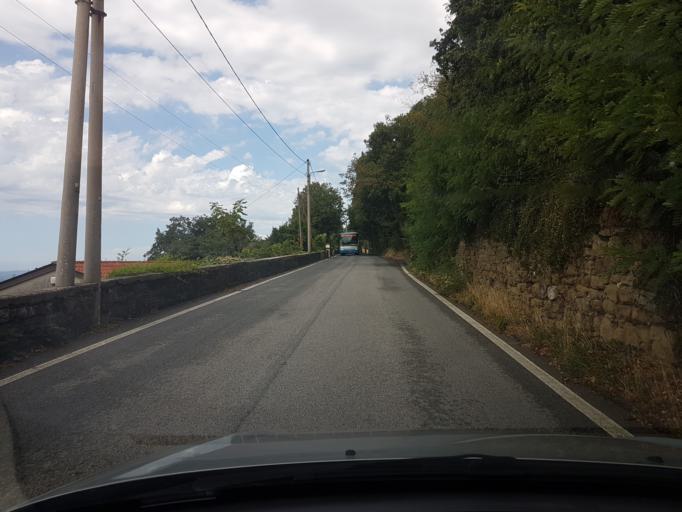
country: IT
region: Friuli Venezia Giulia
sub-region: Provincia di Trieste
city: Prosecco-Contovello
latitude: 45.6900
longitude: 13.7481
